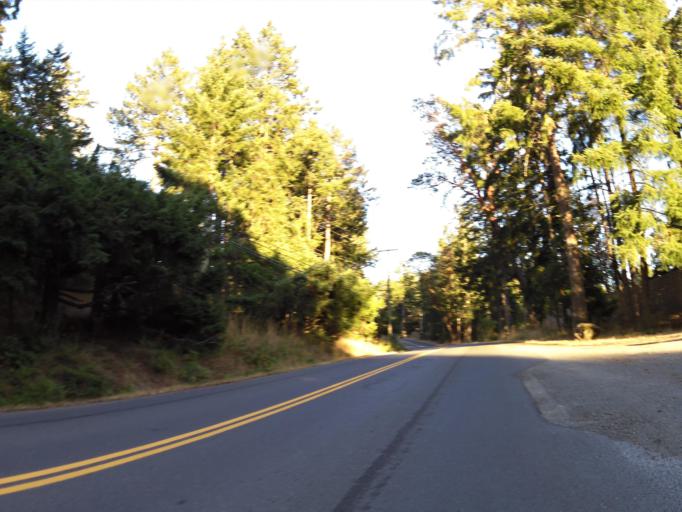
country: CA
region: British Columbia
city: North Cowichan
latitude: 48.8791
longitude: -123.5625
